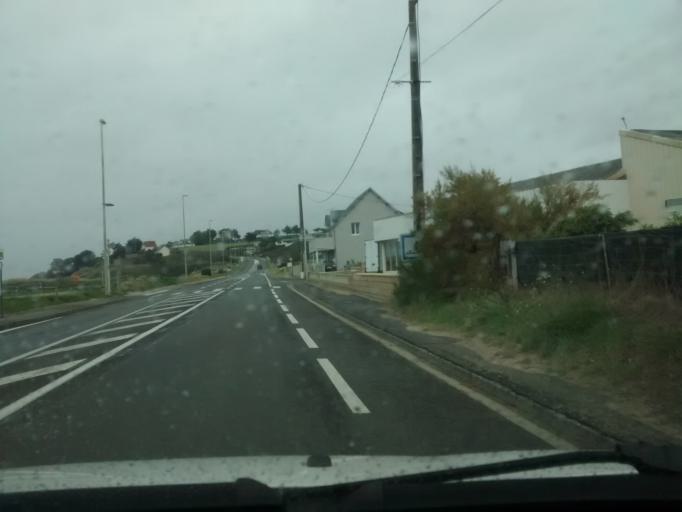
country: FR
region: Lower Normandy
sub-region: Departement de la Manche
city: Saint-Pair-sur-Mer
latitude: 48.8029
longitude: -1.5674
